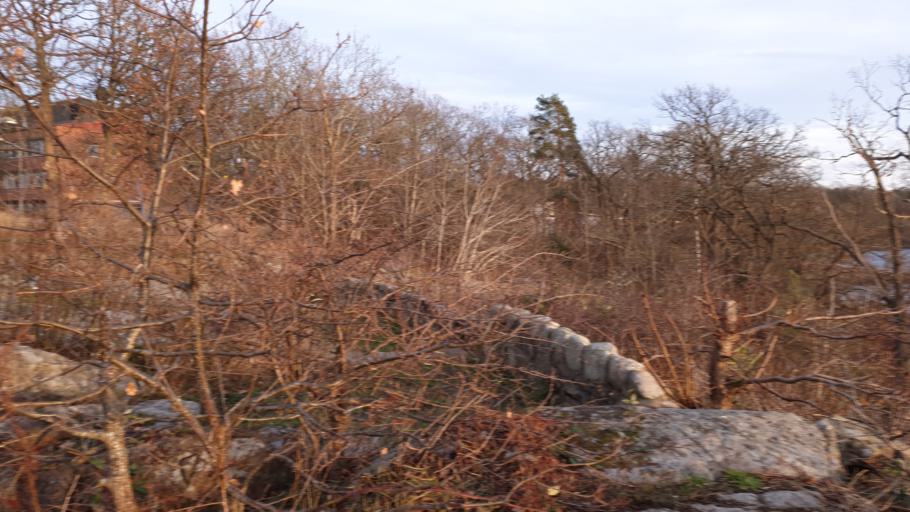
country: SE
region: Blekinge
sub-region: Karlshamns Kommun
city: Karlshamn
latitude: 56.1632
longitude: 14.8718
